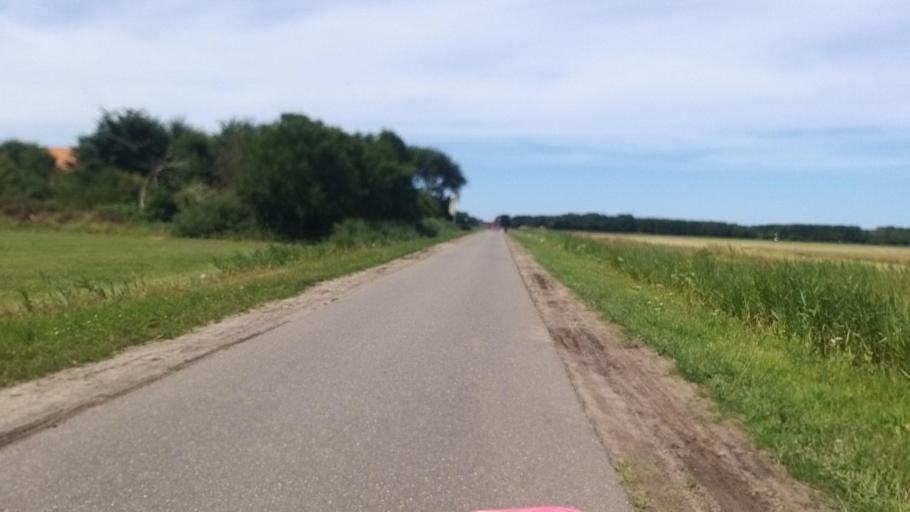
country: NL
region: North Holland
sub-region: Gemeente Texel
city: Den Burg
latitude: 53.1439
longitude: 4.8685
